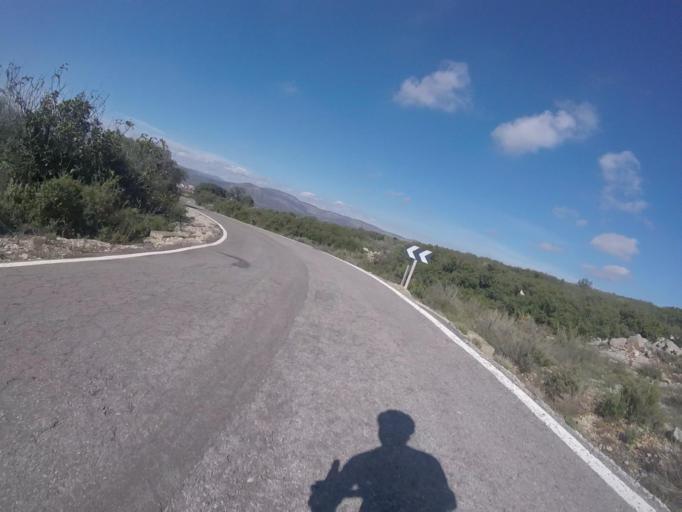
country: ES
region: Valencia
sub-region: Provincia de Castello
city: Albocasser
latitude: 40.3546
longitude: 0.0415
